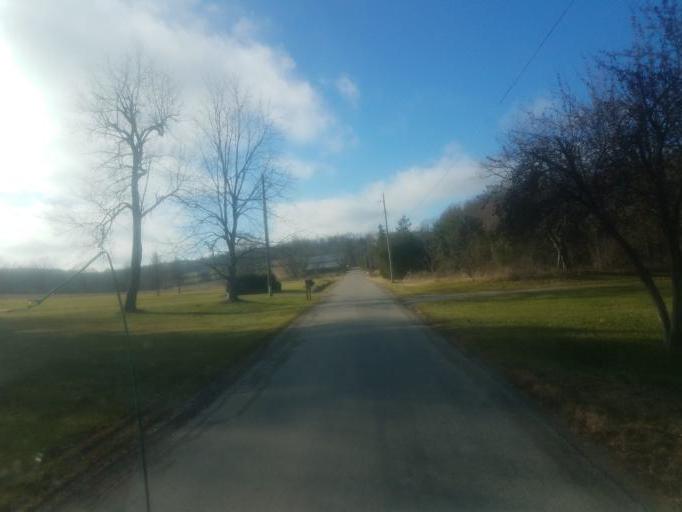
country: US
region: Ohio
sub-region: Sandusky County
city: Bellville
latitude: 40.5828
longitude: -82.5286
